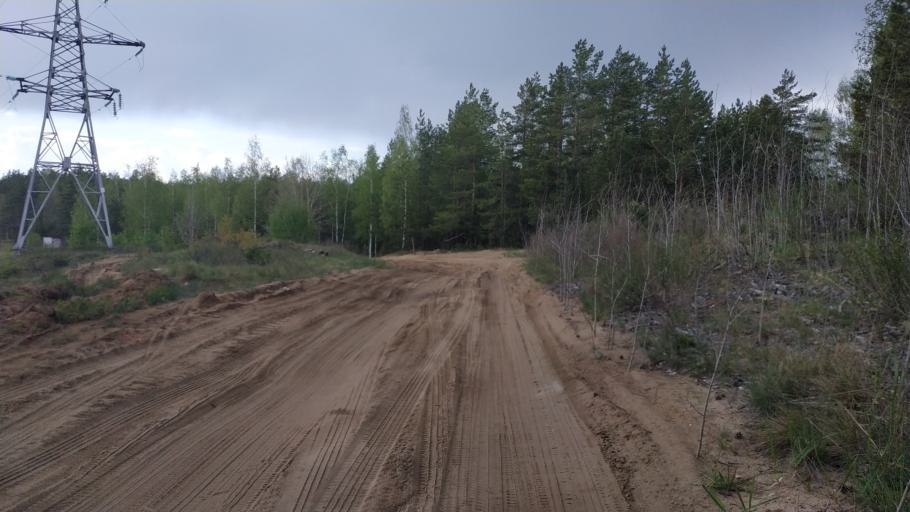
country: RU
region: Chuvashia
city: Novocheboksarsk
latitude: 56.1607
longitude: 47.4638
